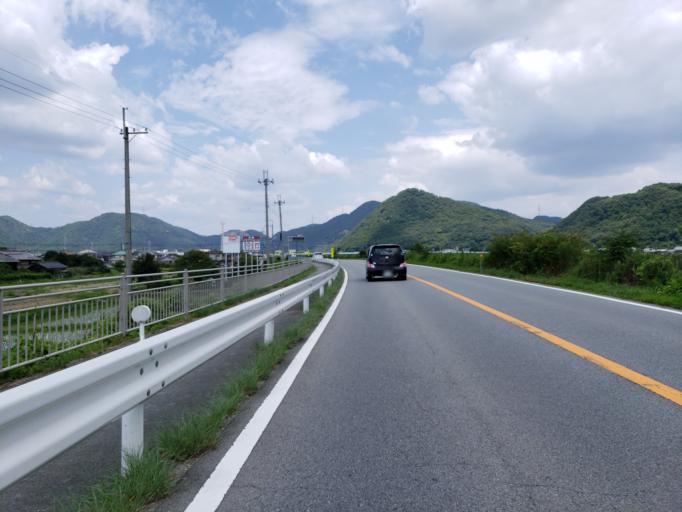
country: JP
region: Hyogo
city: Kariya
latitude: 34.7635
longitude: 134.4179
